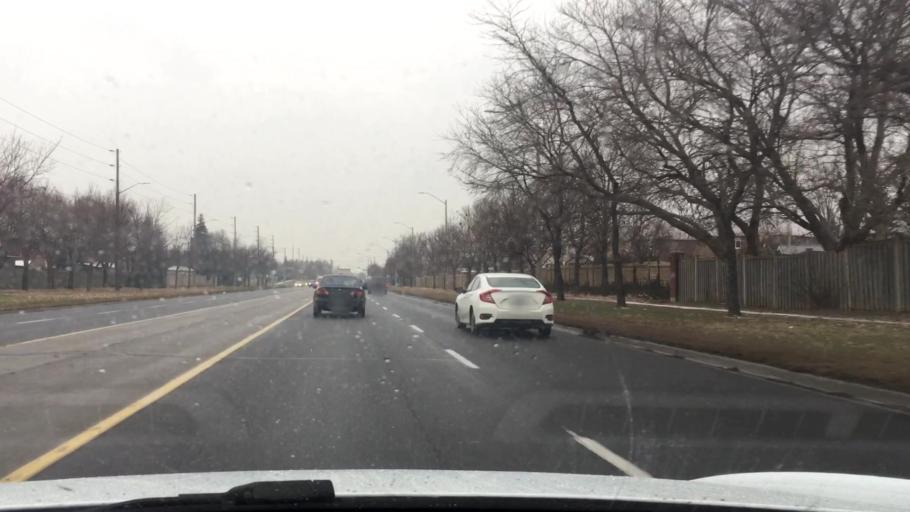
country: CA
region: Ontario
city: Markham
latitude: 43.8436
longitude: -79.2784
